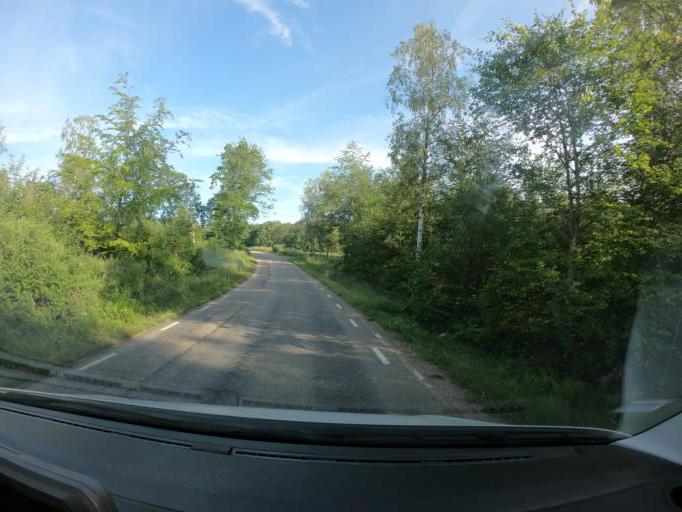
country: SE
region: Skane
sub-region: Angelholms Kommun
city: Munka-Ljungby
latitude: 56.3155
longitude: 12.9906
